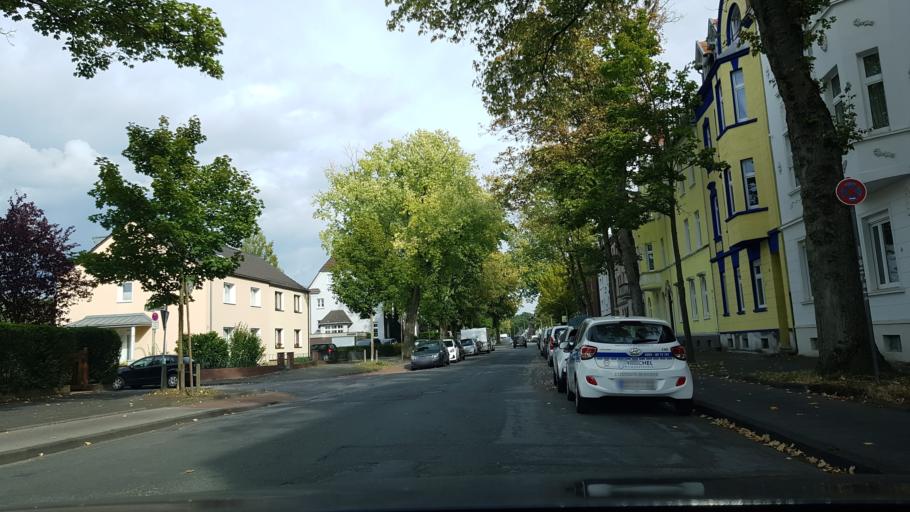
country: DE
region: North Rhine-Westphalia
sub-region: Regierungsbezirk Dusseldorf
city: Hochfeld
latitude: 51.3653
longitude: 6.7813
